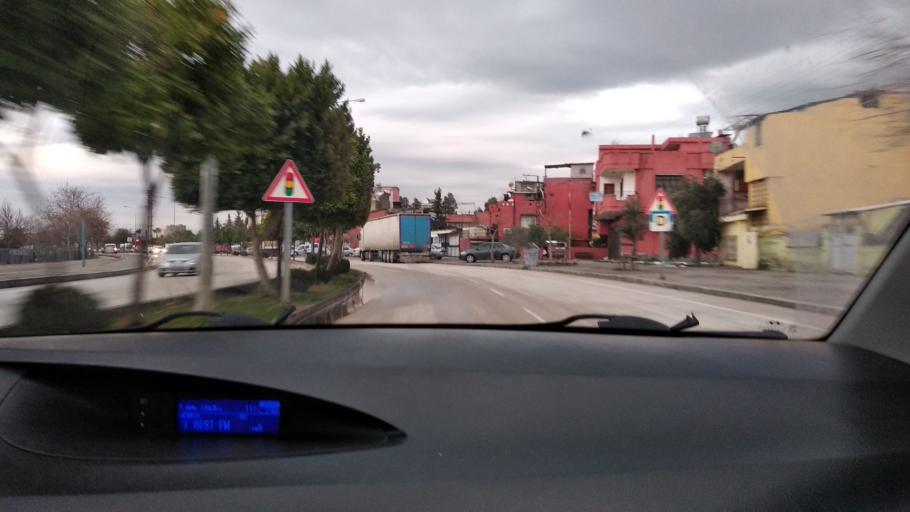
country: TR
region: Adana
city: Yuregir
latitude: 37.0143
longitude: 35.3863
